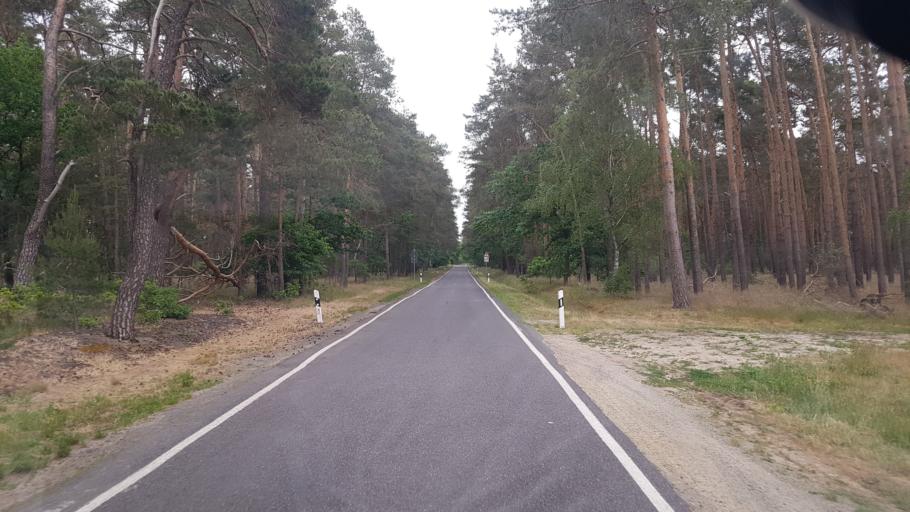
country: DE
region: Brandenburg
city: Herzberg
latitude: 51.7906
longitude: 13.2483
